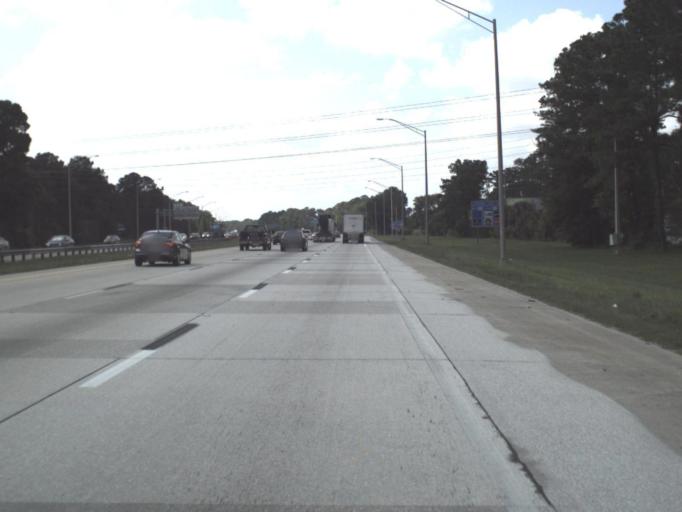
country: US
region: Florida
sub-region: Duval County
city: Jacksonville
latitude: 30.2340
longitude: -81.5796
